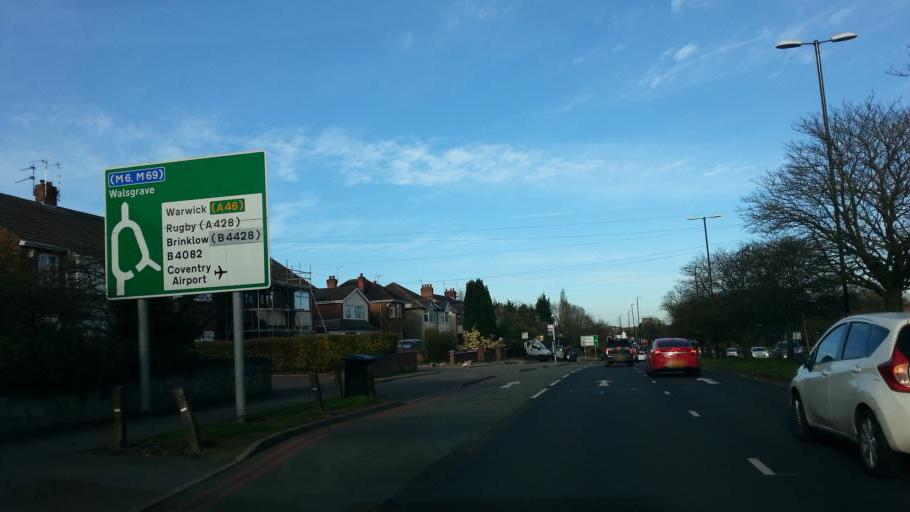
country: GB
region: England
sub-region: Warwickshire
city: Exhall
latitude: 52.4217
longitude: -1.4503
